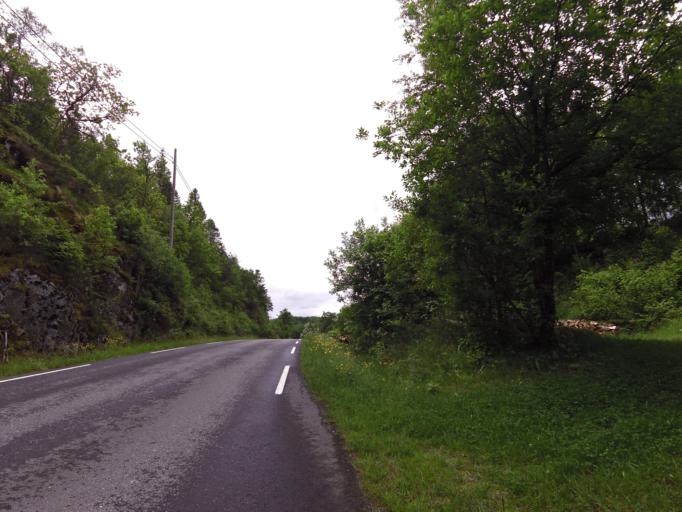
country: NO
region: Vest-Agder
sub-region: Lyngdal
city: Lyngdal
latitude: 58.1036
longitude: 6.9623
